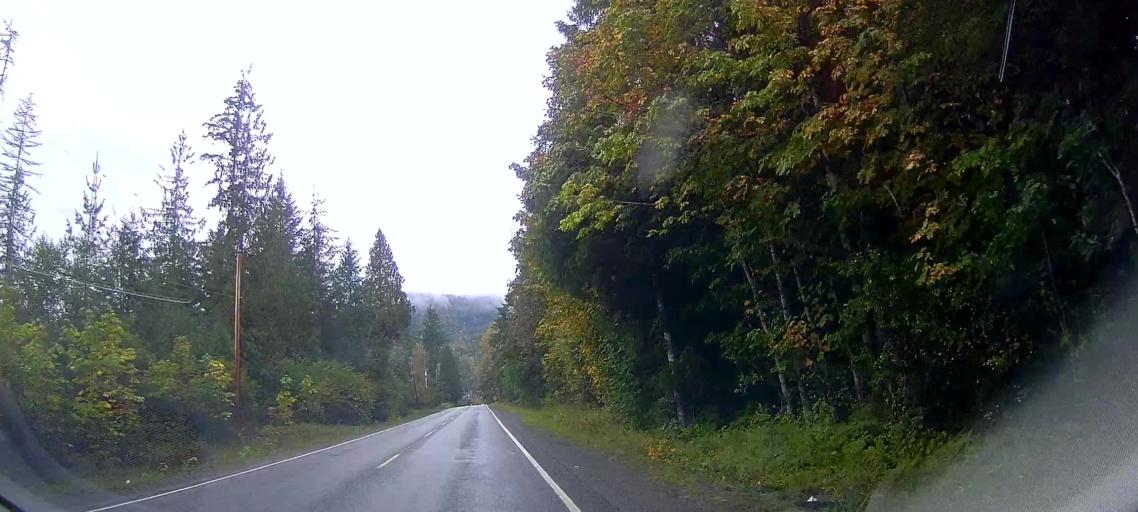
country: US
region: Washington
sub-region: Snohomish County
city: Darrington
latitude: 48.5314
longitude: -121.7661
